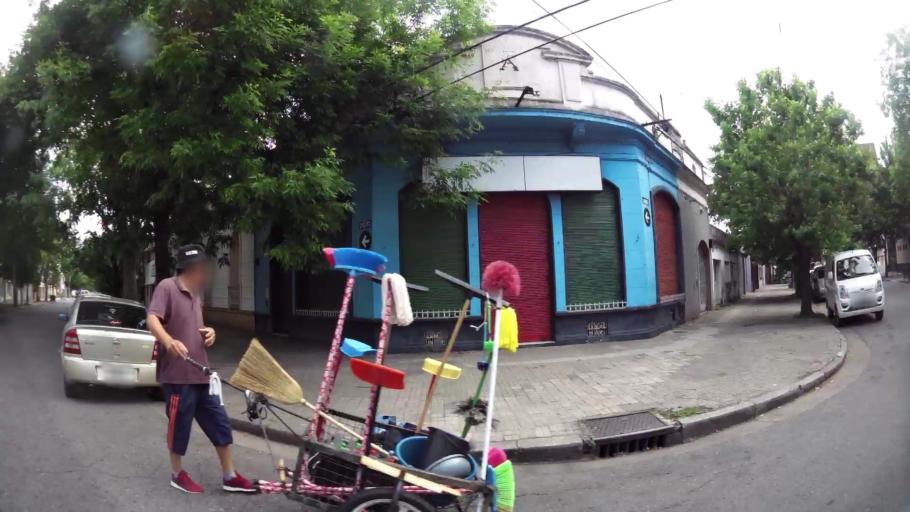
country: AR
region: Santa Fe
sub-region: Departamento de Rosario
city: Rosario
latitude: -32.9688
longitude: -60.6438
